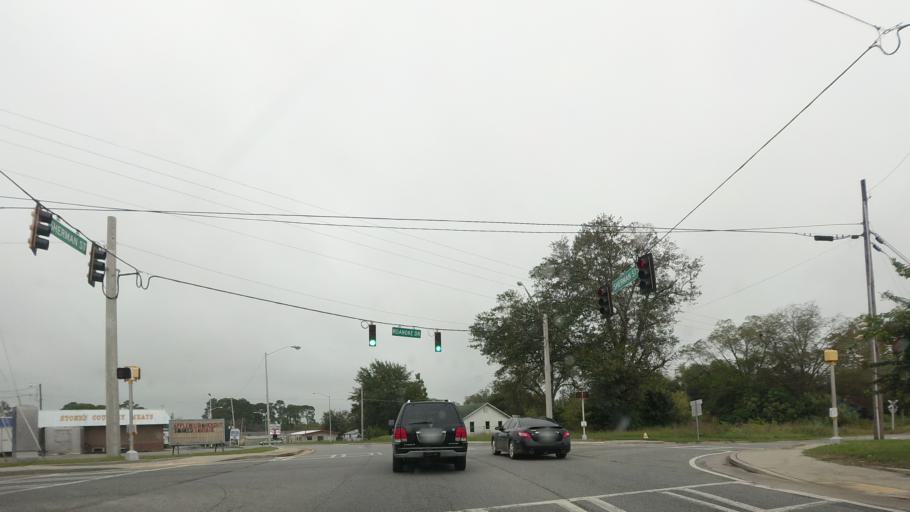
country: US
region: Georgia
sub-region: Ben Hill County
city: Fitzgerald
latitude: 31.7058
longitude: -83.2517
